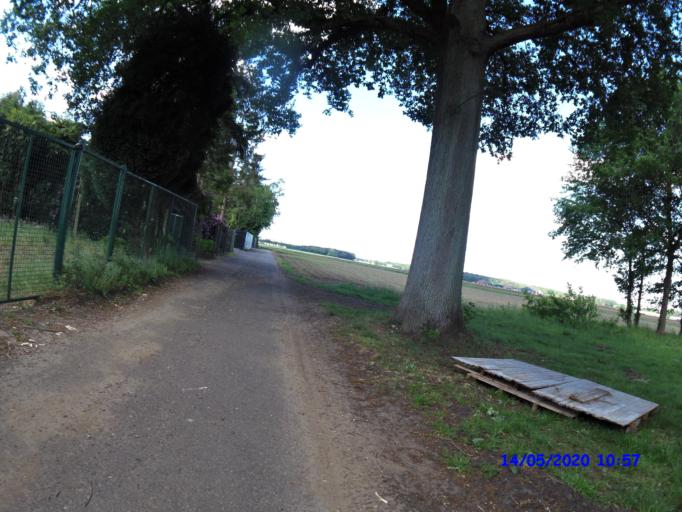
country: BE
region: Flanders
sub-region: Provincie Antwerpen
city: Lille
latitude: 51.2350
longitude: 4.8828
